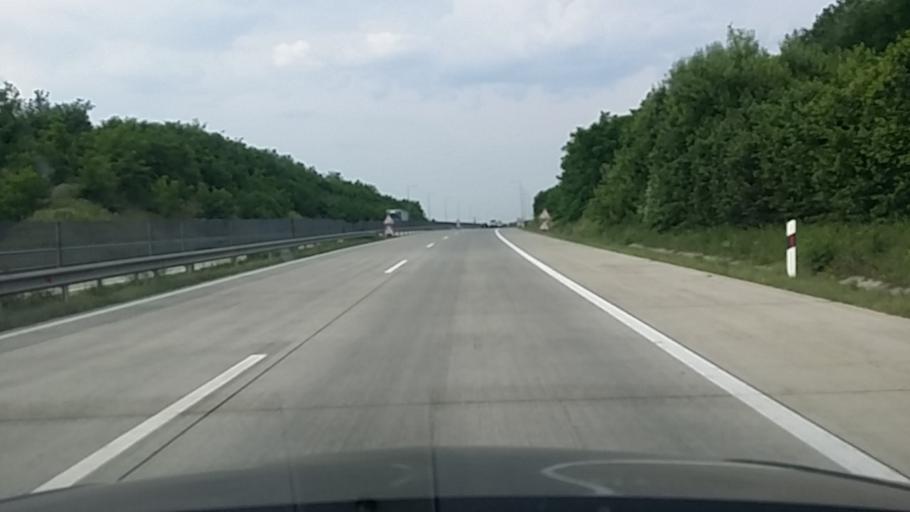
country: HU
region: Pest
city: Kerepes
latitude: 47.5623
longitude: 19.3197
